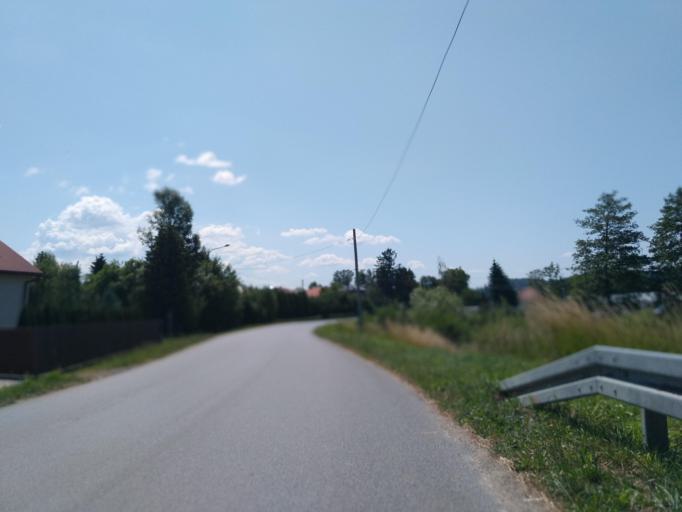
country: PL
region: Subcarpathian Voivodeship
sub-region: Powiat sanocki
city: Niebieszczany
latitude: 49.5299
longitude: 22.1275
